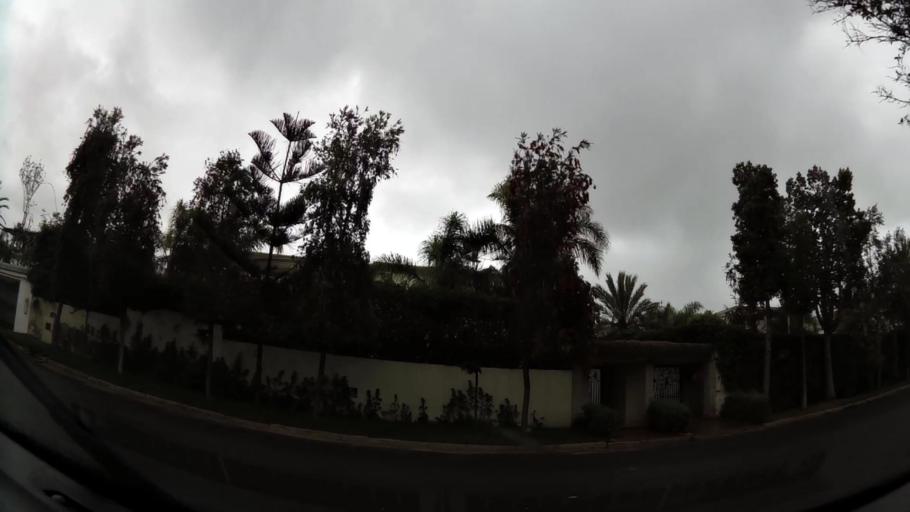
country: MA
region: Grand Casablanca
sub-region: Casablanca
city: Casablanca
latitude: 33.5330
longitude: -7.6204
